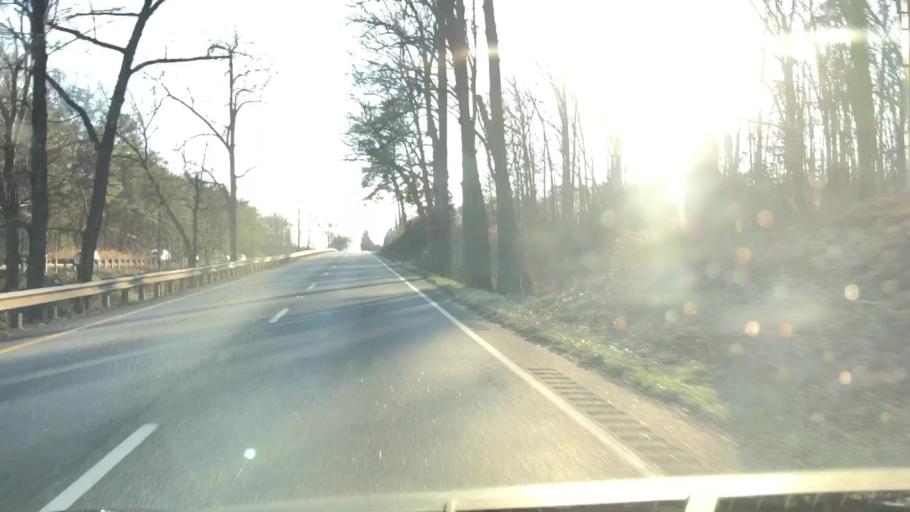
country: US
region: Virginia
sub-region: Greene County
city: Ruckersville
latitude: 38.1782
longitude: -78.4058
